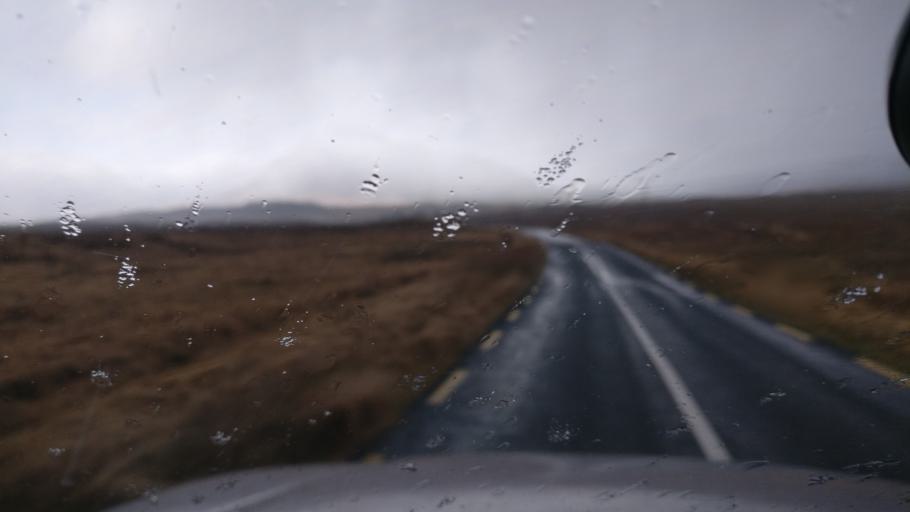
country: IE
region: Connaught
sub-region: County Galway
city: Clifden
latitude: 53.4440
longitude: -9.7696
